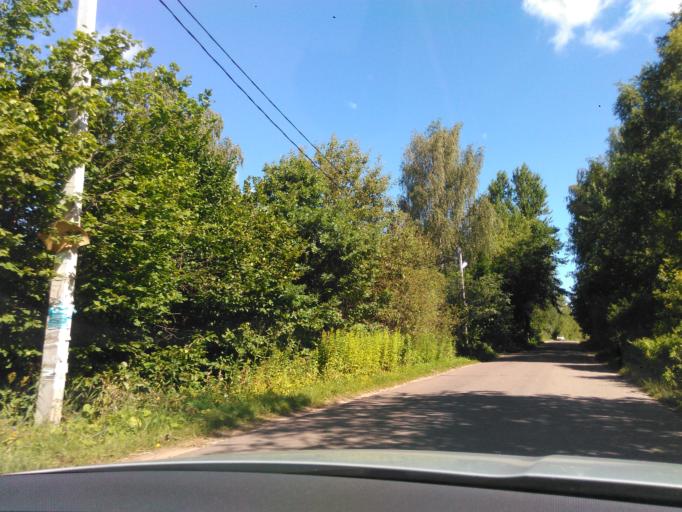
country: RU
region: Moskovskaya
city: Klin
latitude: 56.2253
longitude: 36.8083
